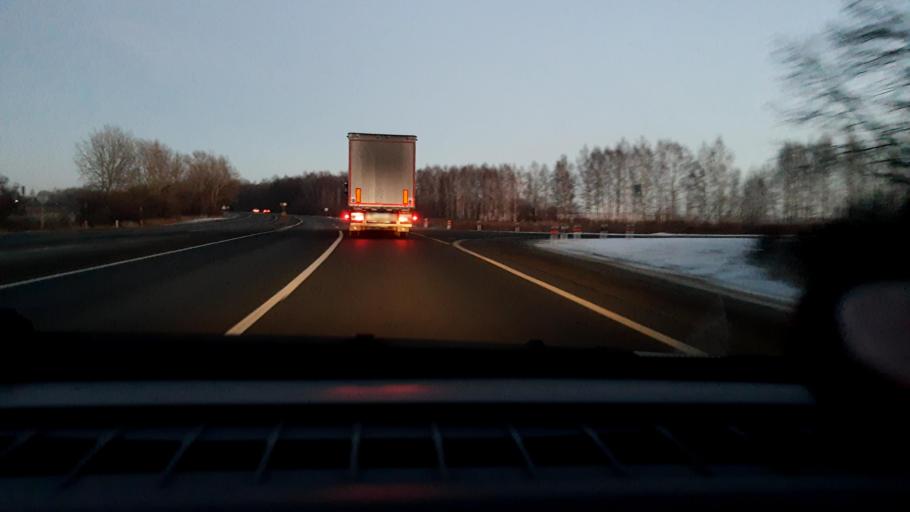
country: RU
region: Nizjnij Novgorod
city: Lyskovo
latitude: 56.0088
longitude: 44.9363
